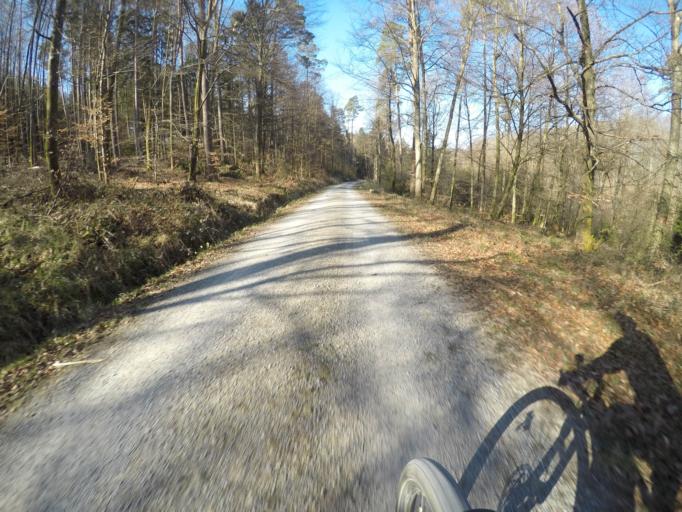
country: DE
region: Baden-Wuerttemberg
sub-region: Tuebingen Region
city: Dettenhausen
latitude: 48.6065
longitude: 9.1133
